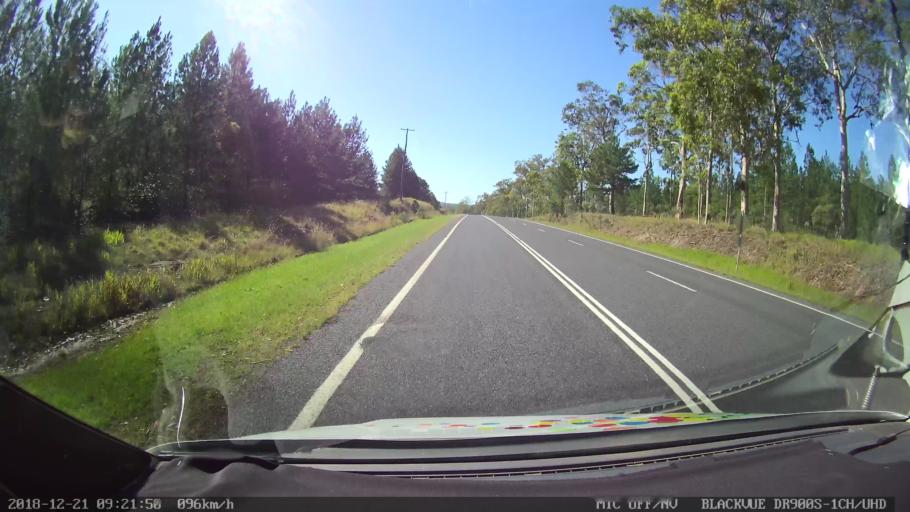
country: AU
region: New South Wales
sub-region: Clarence Valley
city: Maclean
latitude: -29.3344
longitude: 153.0006
